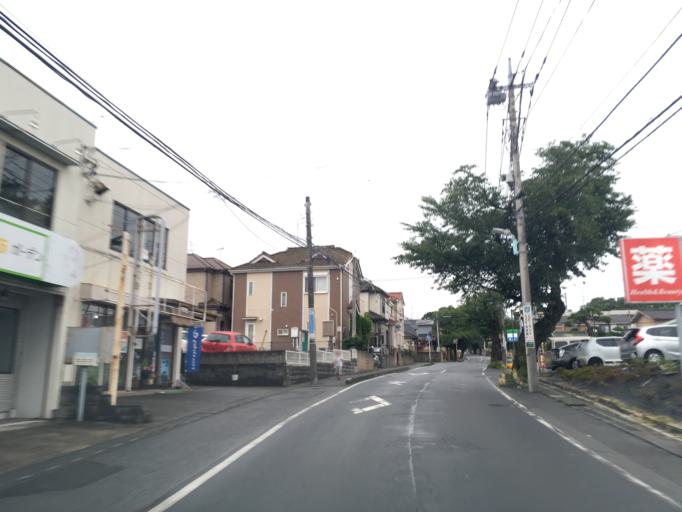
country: JP
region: Saitama
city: Tokorozawa
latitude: 35.7874
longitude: 139.4395
